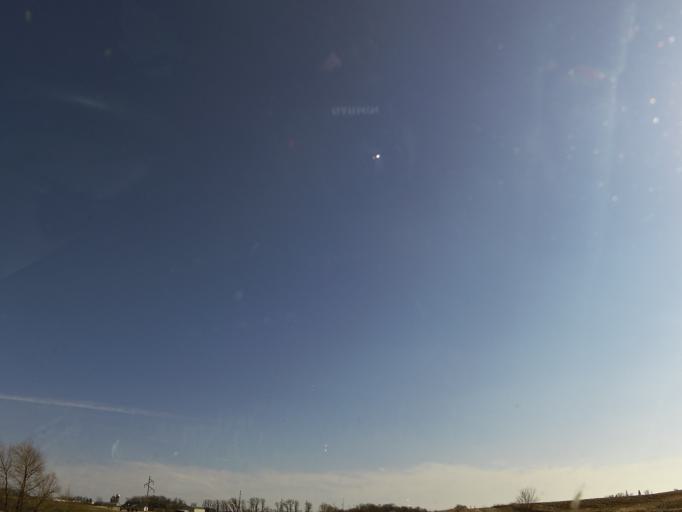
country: US
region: Minnesota
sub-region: Steele County
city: Owatonna
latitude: 44.0309
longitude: -93.2471
